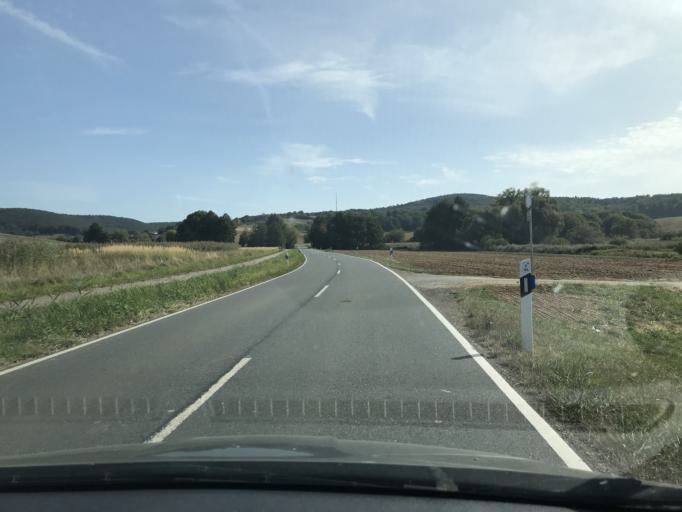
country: DE
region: Hesse
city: Gross-Umstadt
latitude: 49.8425
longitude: 8.9458
